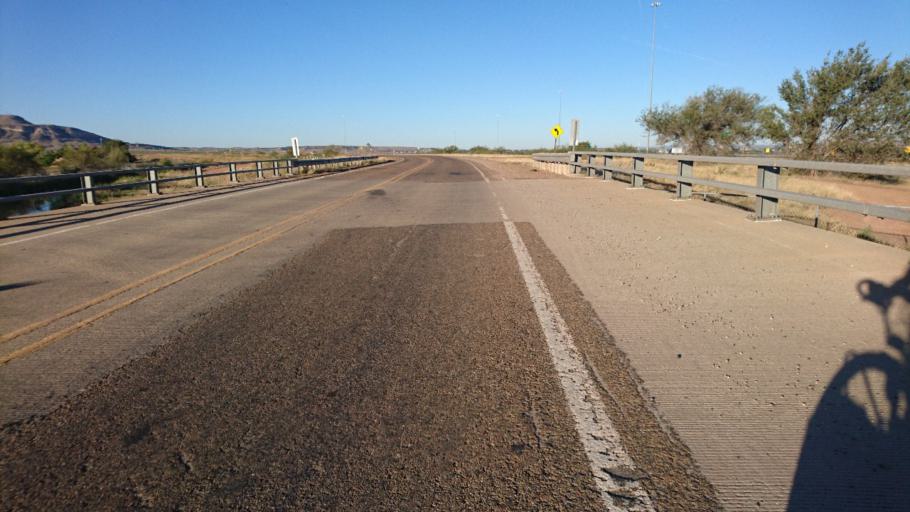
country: US
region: New Mexico
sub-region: Quay County
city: Tucumcari
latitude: 35.1716
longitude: -103.6685
